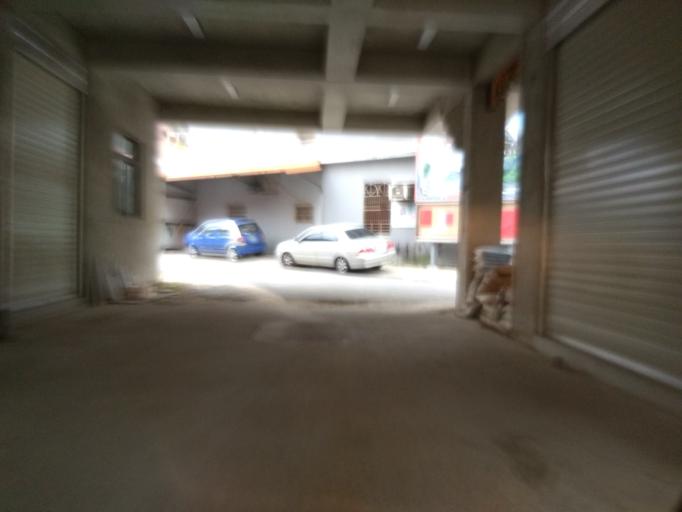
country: TW
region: Taiwan
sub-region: Hsinchu
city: Hsinchu
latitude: 24.7931
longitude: 120.9220
